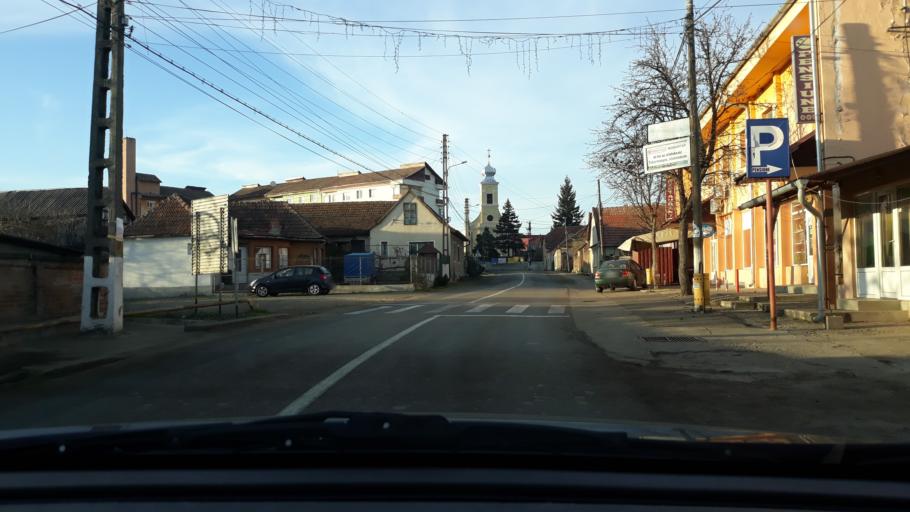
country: RO
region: Bihor
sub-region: Comuna Suplacu de Barcau
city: Suplacu de Barcau
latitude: 47.2579
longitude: 22.5274
